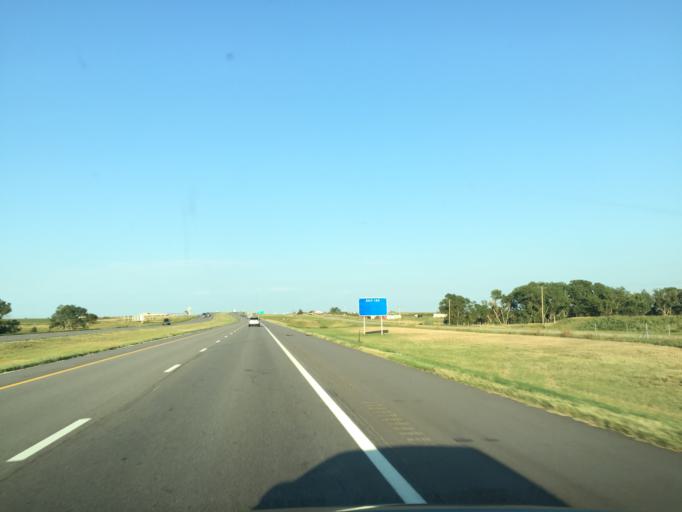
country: US
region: Kansas
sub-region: Russell County
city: Russell
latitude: 38.8569
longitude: -98.7205
